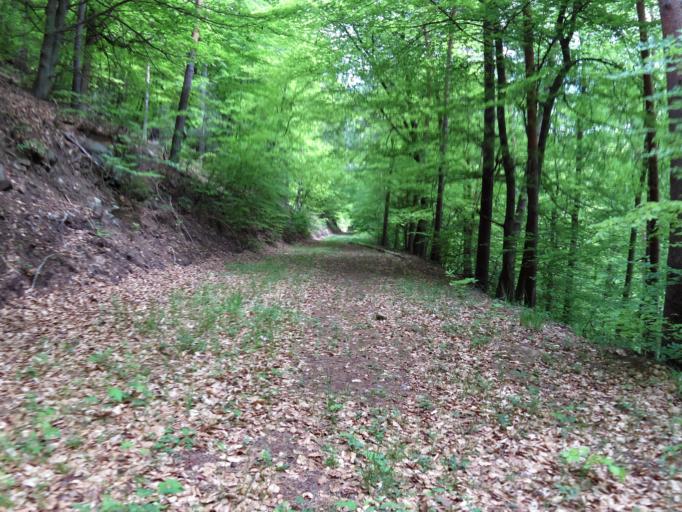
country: DE
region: Rheinland-Pfalz
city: Neidenfels
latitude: 49.4101
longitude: 8.0331
